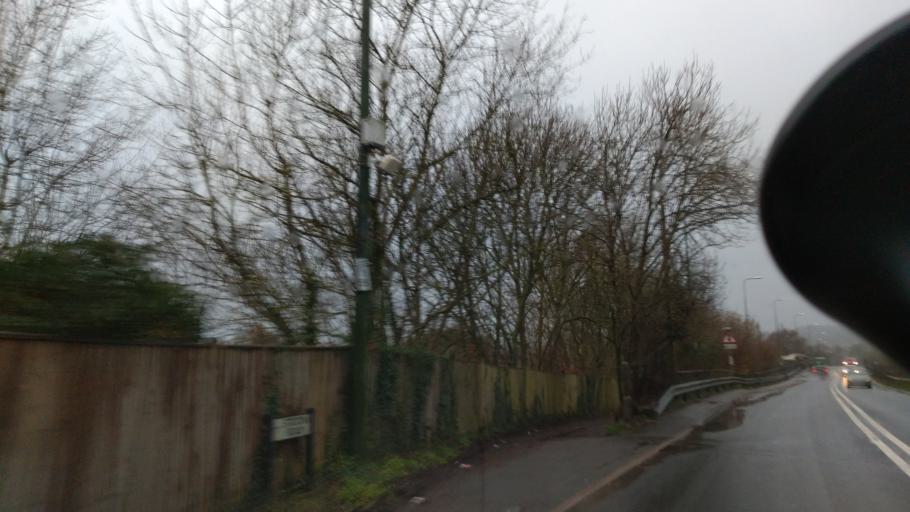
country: GB
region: England
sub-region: West Sussex
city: Arundel
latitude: 50.8474
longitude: -0.5448
